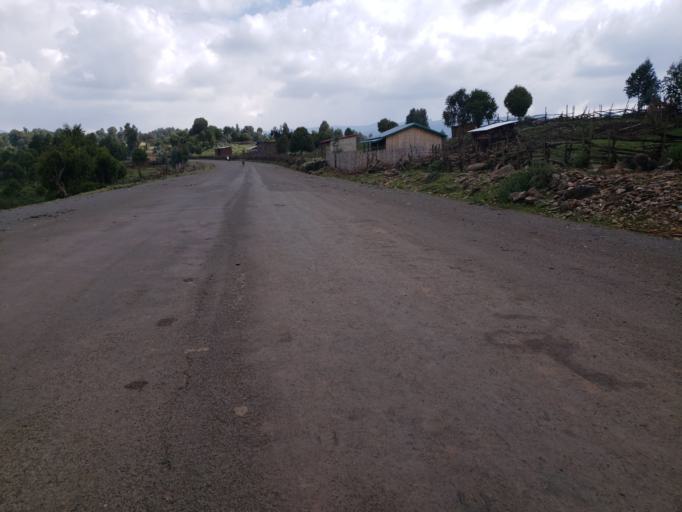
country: ET
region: Oromiya
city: Dodola
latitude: 6.8751
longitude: 39.3856
